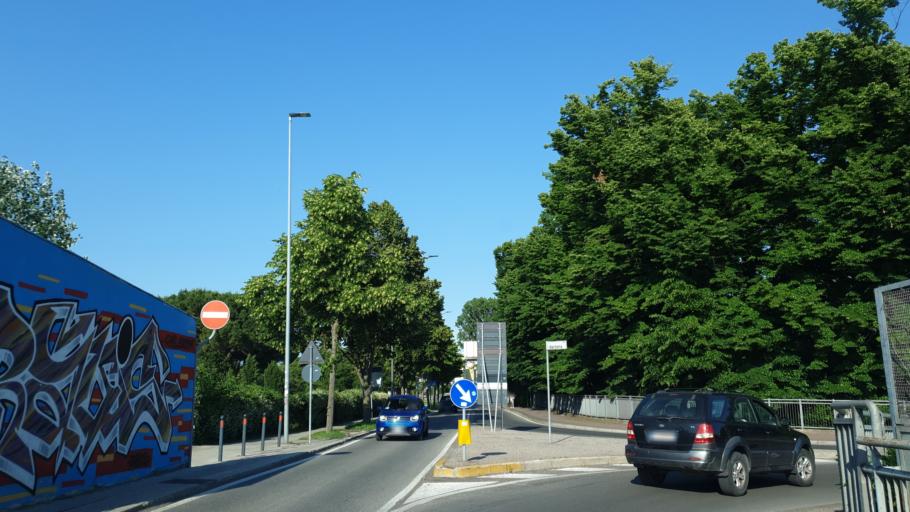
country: IT
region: Emilia-Romagna
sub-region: Provincia di Ravenna
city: Ravenna
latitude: 44.4239
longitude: 12.2073
